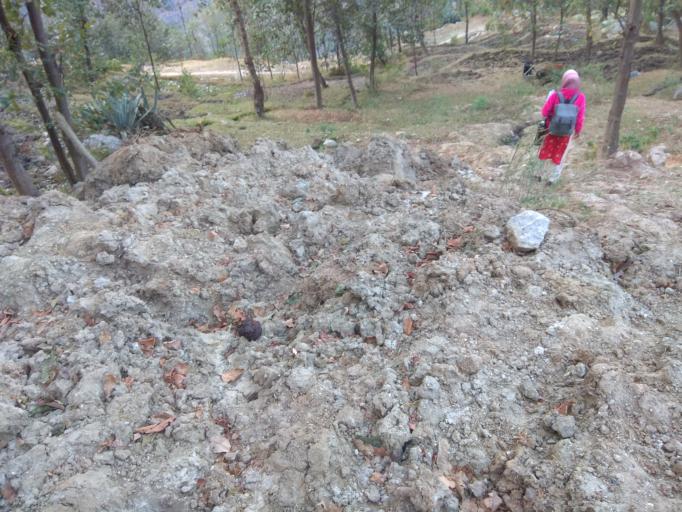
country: NP
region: Far Western
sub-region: Seti Zone
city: Achham
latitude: 29.2319
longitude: 81.6451
